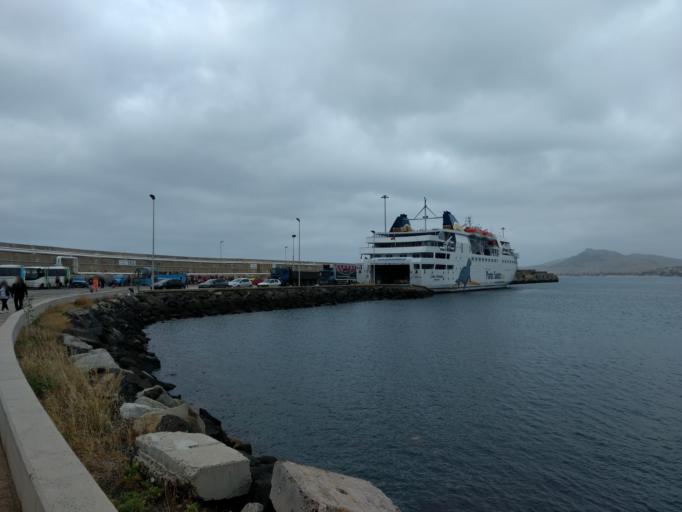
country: PT
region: Madeira
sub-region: Porto Santo
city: Vila de Porto Santo
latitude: 33.0597
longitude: -16.3104
